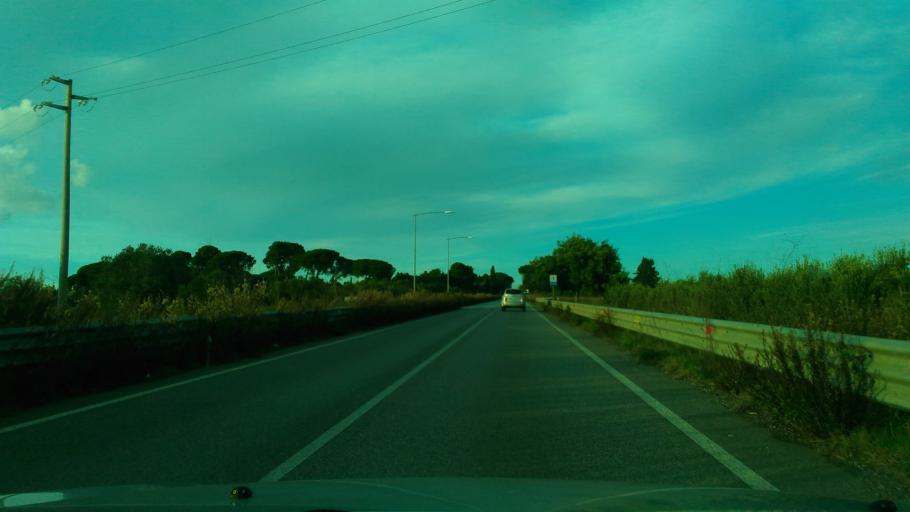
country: IT
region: Tuscany
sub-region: Provincia di Livorno
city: S.P. in Palazzi
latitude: 43.3351
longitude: 10.5059
